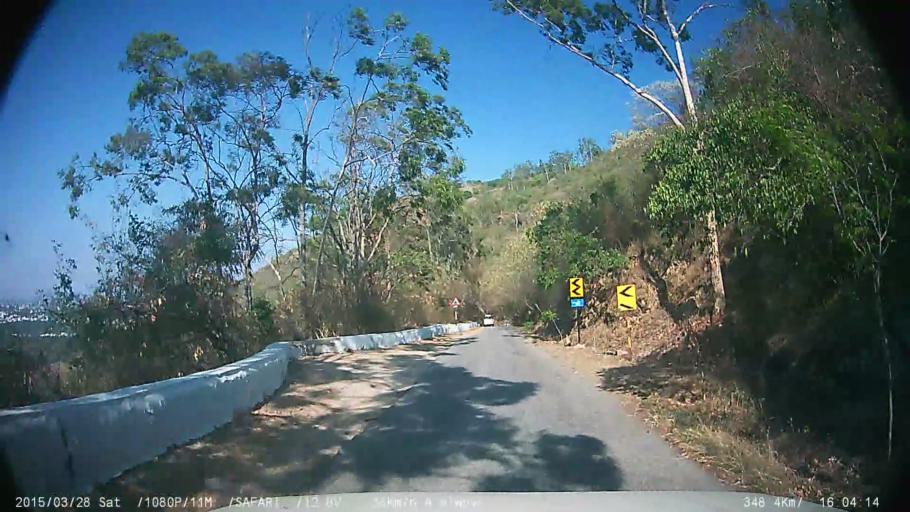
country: IN
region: Karnataka
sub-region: Mysore
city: Mysore
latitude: 12.2811
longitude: 76.6742
